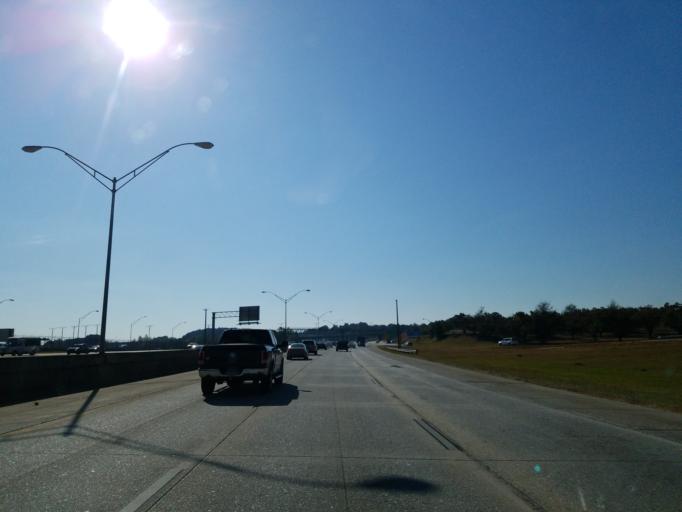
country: US
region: Georgia
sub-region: Fulton County
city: College Park
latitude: 33.6511
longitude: -84.4412
